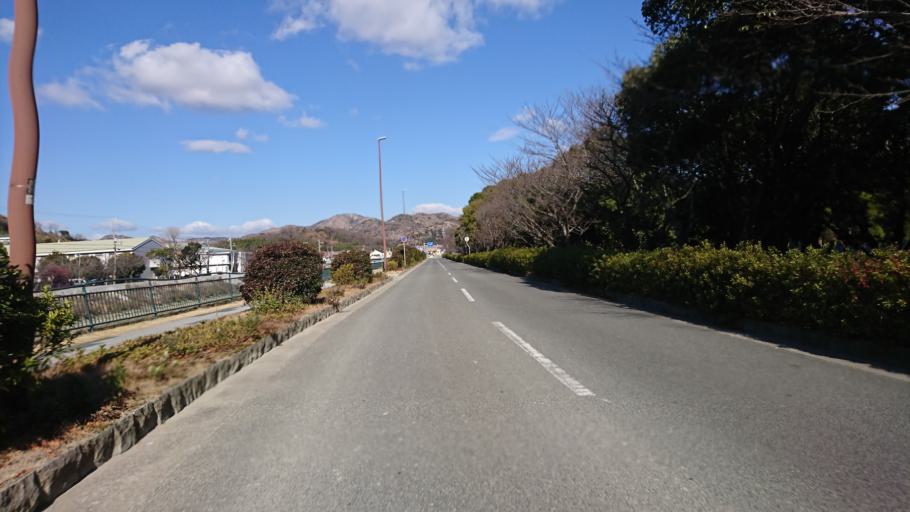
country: JP
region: Hyogo
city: Kakogawacho-honmachi
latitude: 34.7804
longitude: 134.7978
